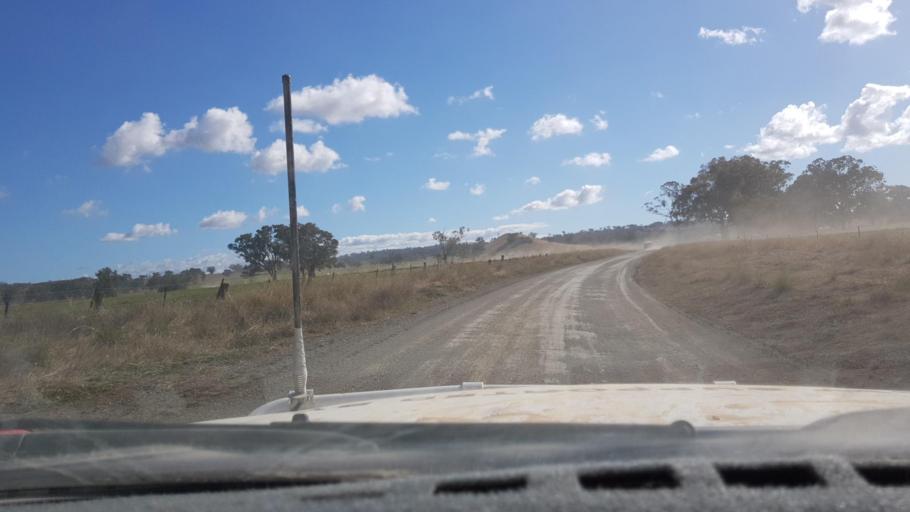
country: AU
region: New South Wales
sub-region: Tamworth Municipality
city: Manilla
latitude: -30.5888
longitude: 150.4892
